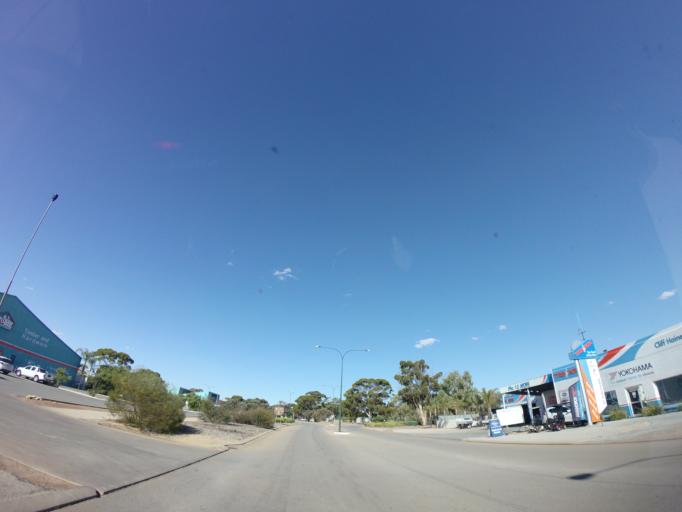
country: AU
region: Western Australia
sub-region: Merredin
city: Merredin
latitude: -31.4820
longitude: 118.2822
